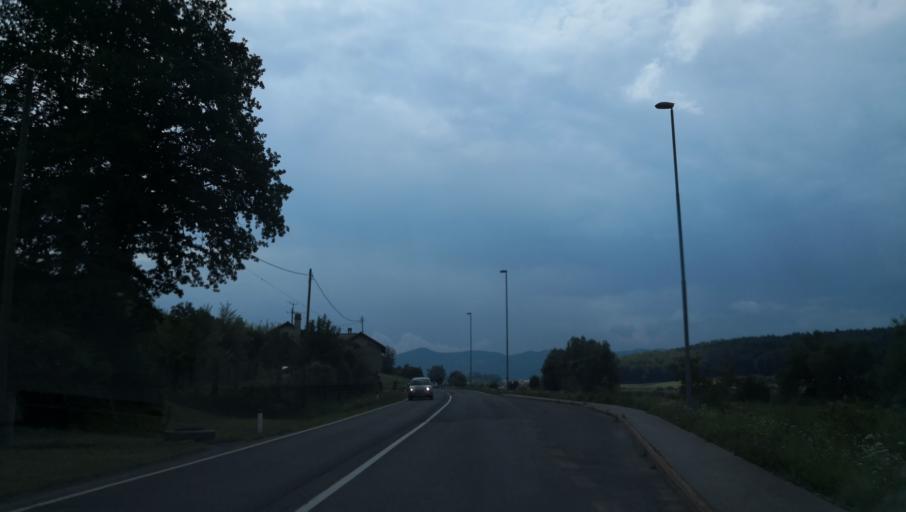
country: SI
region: Ivancna Gorica
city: Ivancna Gorica
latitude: 45.9263
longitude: 14.8051
